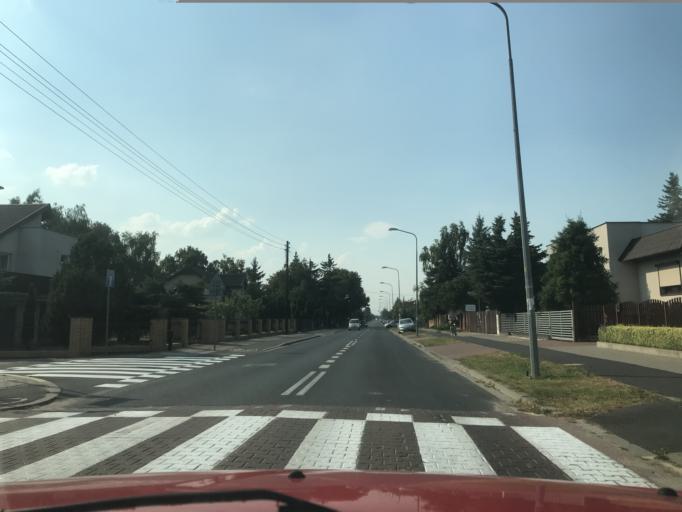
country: PL
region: Greater Poland Voivodeship
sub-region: Powiat poznanski
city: Plewiska
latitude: 52.3814
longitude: 16.8176
